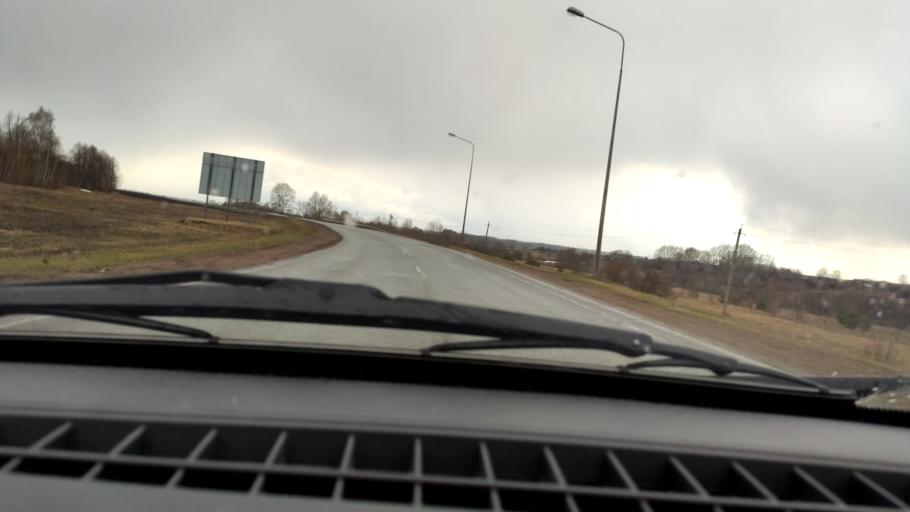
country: RU
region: Bashkortostan
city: Kushnarenkovo
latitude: 55.0736
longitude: 55.2655
